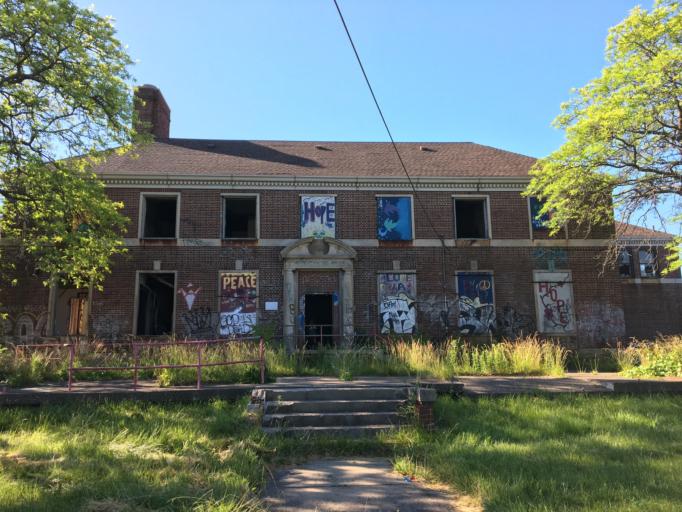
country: US
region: Michigan
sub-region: Wayne County
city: Dearborn
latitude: 42.3436
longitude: -83.1201
